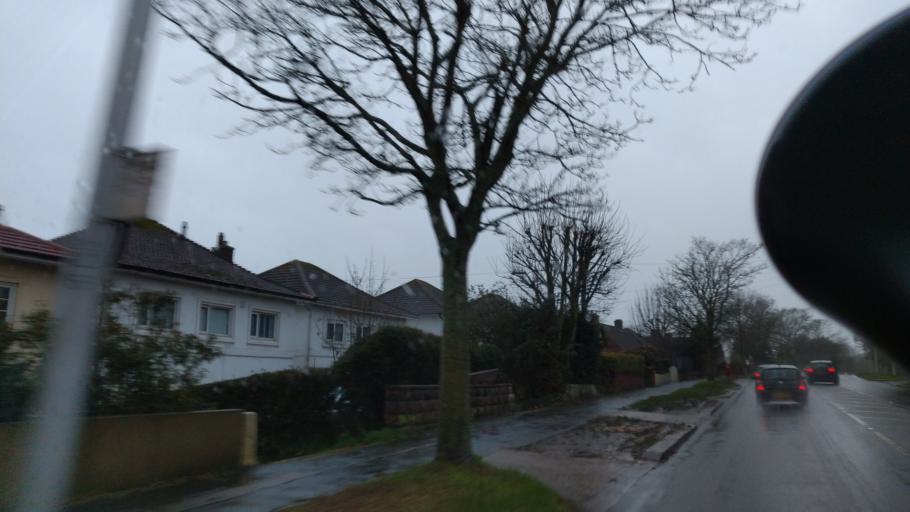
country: GB
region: England
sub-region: West Sussex
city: Findon
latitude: 50.8407
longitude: -0.4036
